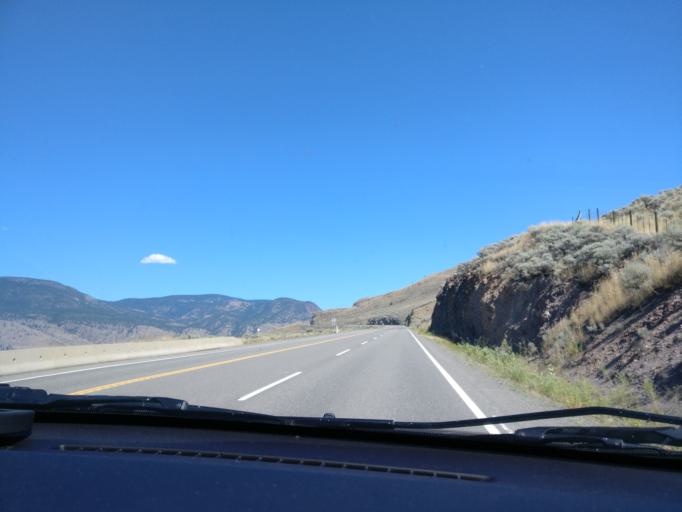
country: CA
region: British Columbia
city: Logan Lake
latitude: 50.7644
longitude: -120.7888
